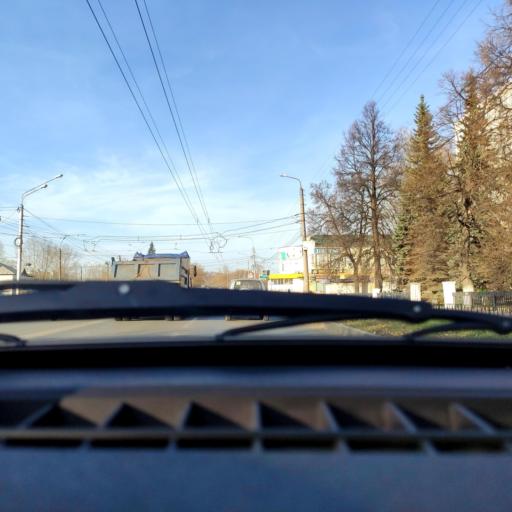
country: RU
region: Bashkortostan
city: Ufa
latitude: 54.7966
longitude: 56.1393
